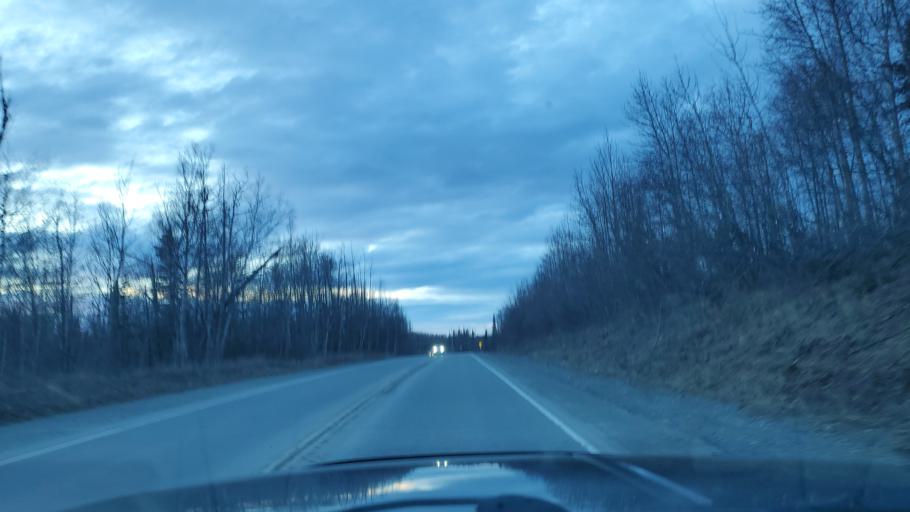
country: US
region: Alaska
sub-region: Matanuska-Susitna Borough
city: Lakes
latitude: 61.6059
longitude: -149.3441
